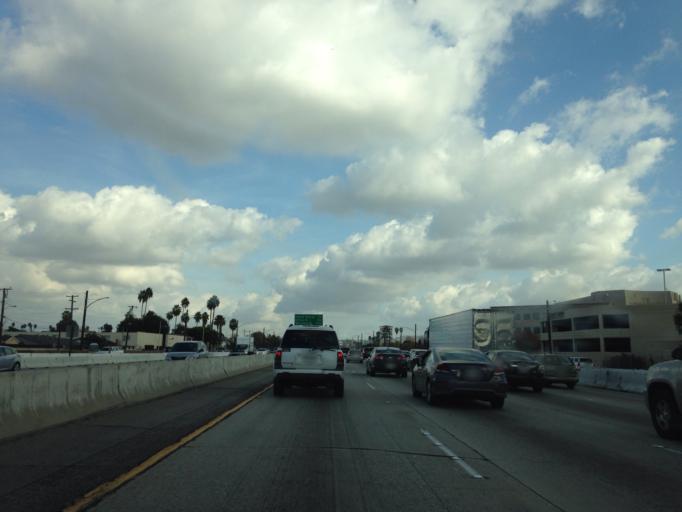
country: US
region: California
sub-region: Los Angeles County
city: West Covina
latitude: 34.0724
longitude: -117.9281
